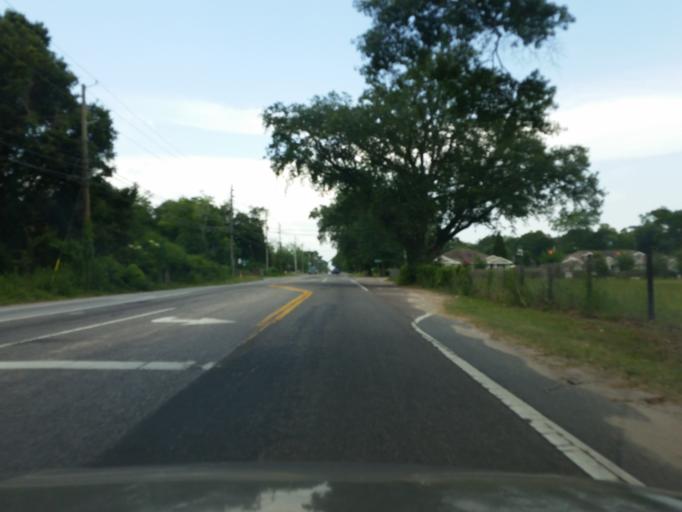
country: US
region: Florida
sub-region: Escambia County
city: Ferry Pass
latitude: 30.5109
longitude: -87.2380
